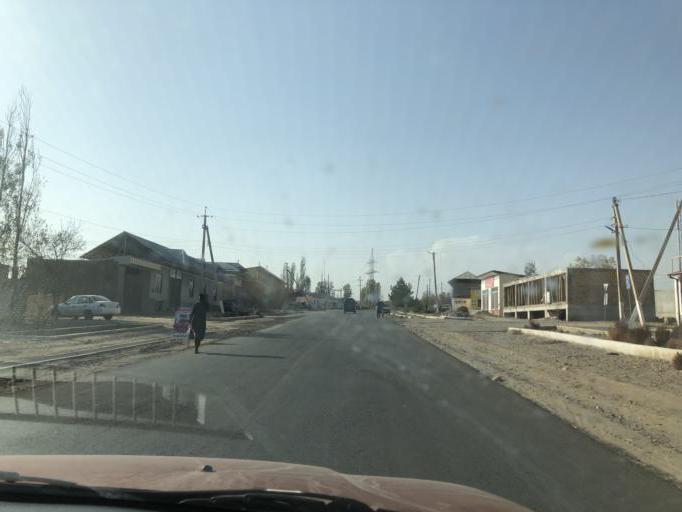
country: UZ
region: Namangan
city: Chust Shahri
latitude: 41.0738
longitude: 71.2018
